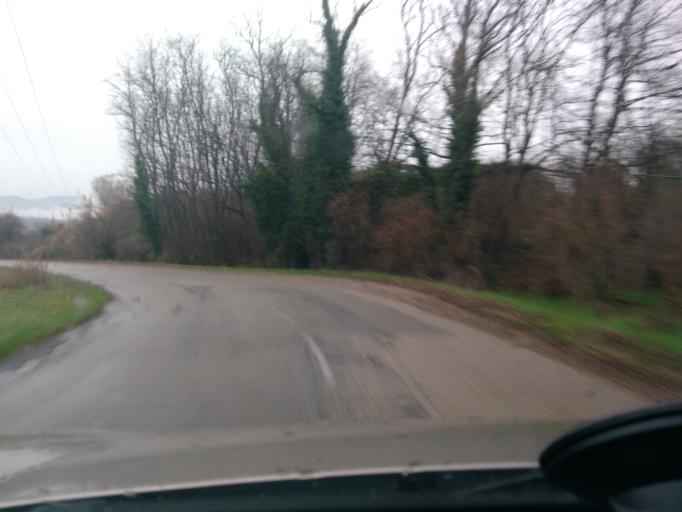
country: FR
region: Rhone-Alpes
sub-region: Departement de la Drome
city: Montelimar
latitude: 44.5393
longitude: 4.7200
